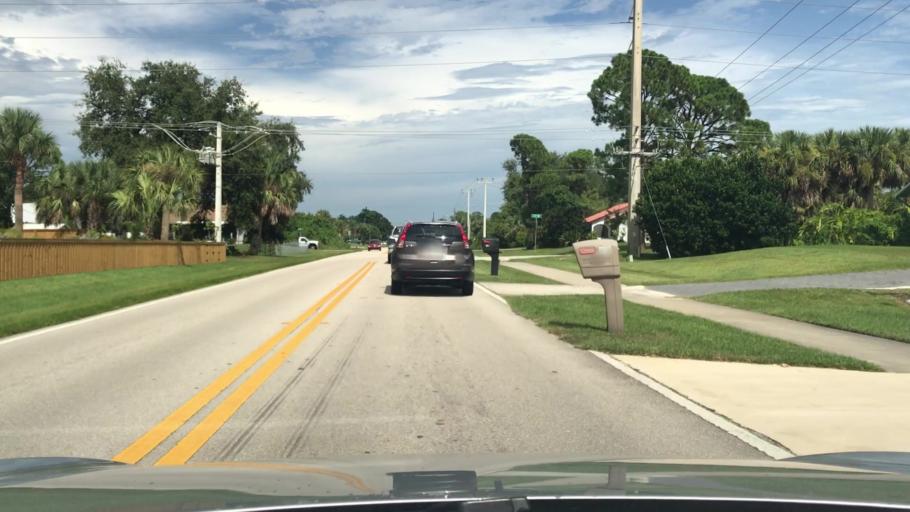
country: US
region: Florida
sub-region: Indian River County
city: Sebastian
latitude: 27.7602
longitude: -80.4707
